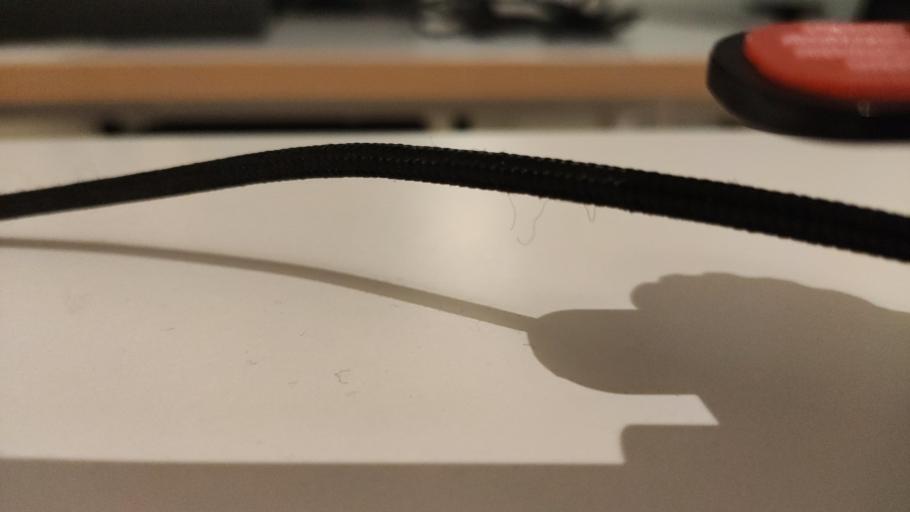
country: RU
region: Moskovskaya
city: Malino
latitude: 55.1083
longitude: 38.1178
